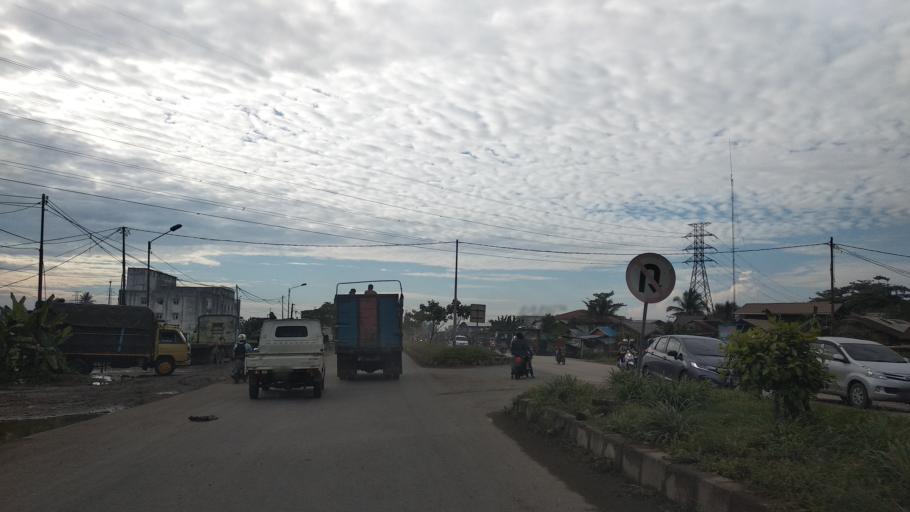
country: ID
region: South Kalimantan
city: Banjarmasin
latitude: -3.3347
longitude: 114.5652
